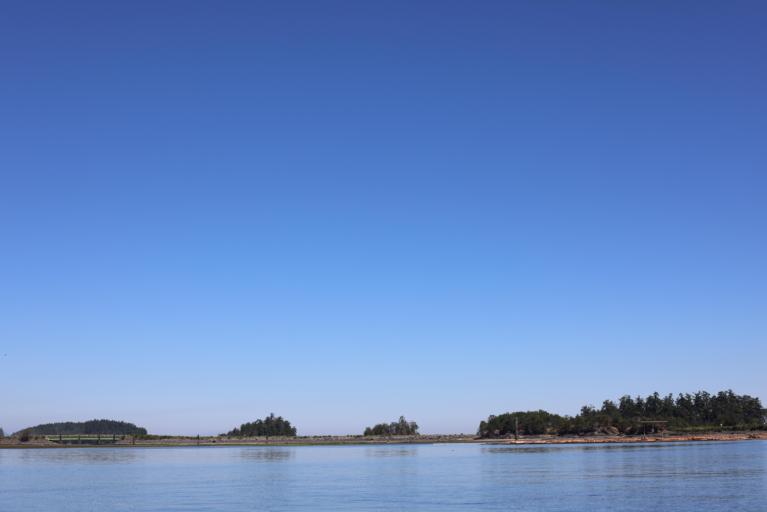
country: CA
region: British Columbia
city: North Cowichan
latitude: 48.8779
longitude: -123.6379
